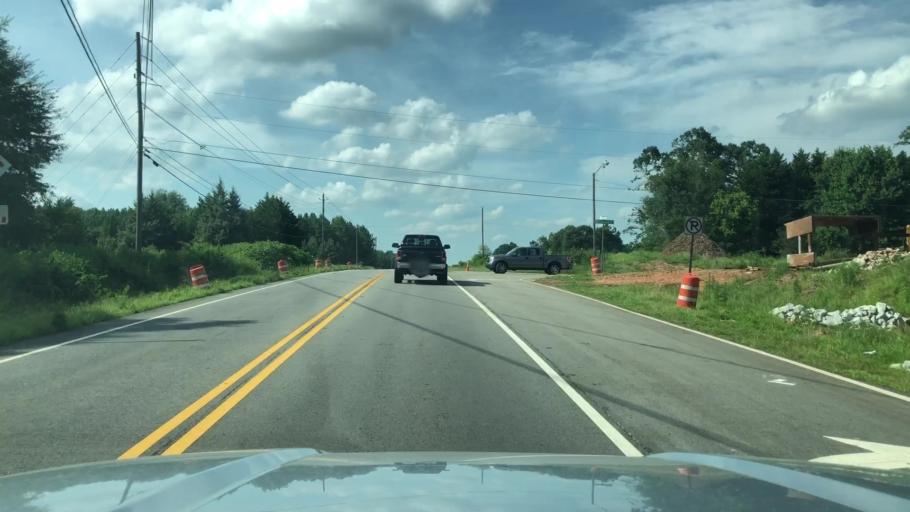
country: US
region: Georgia
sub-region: Paulding County
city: Hiram
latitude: 33.8238
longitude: -84.7590
